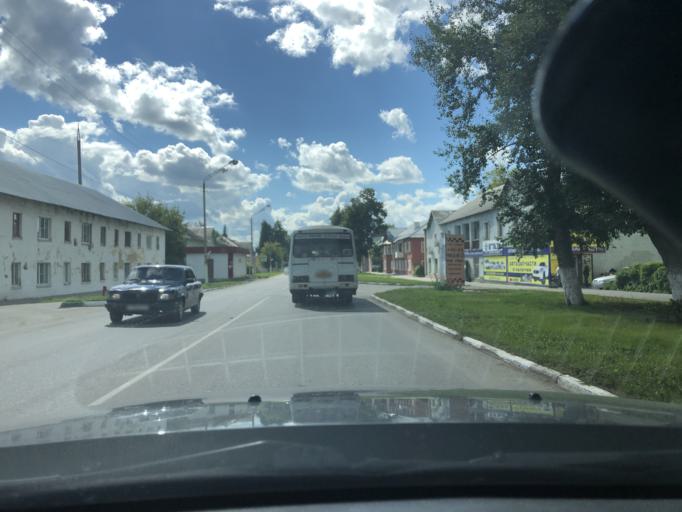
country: RU
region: Tula
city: Kimovsk
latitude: 53.9731
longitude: 38.5204
